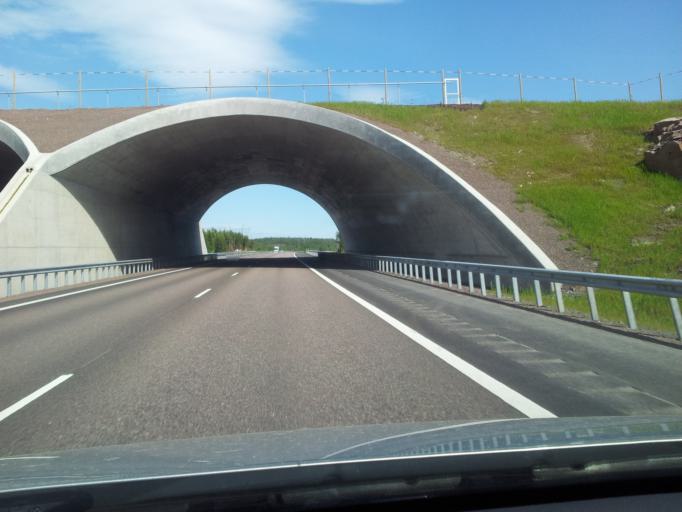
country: FI
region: Uusimaa
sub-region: Loviisa
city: Lovisa
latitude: 60.4899
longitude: 26.3263
